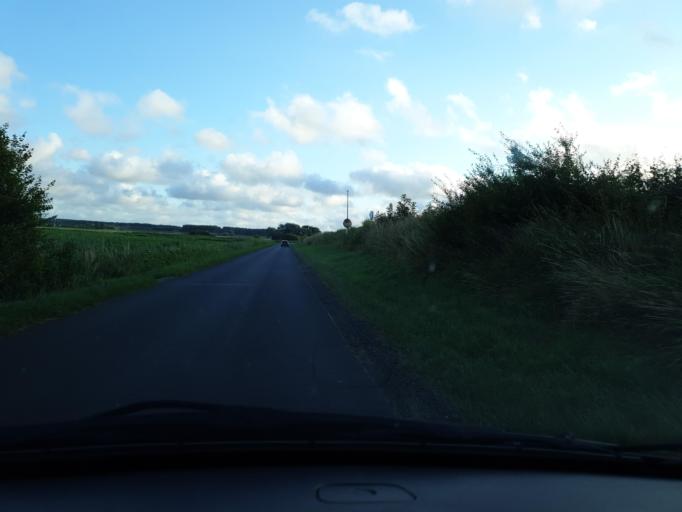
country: DE
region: Schleswig-Holstein
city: Elpersbuttel
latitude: 54.0776
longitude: 9.0255
